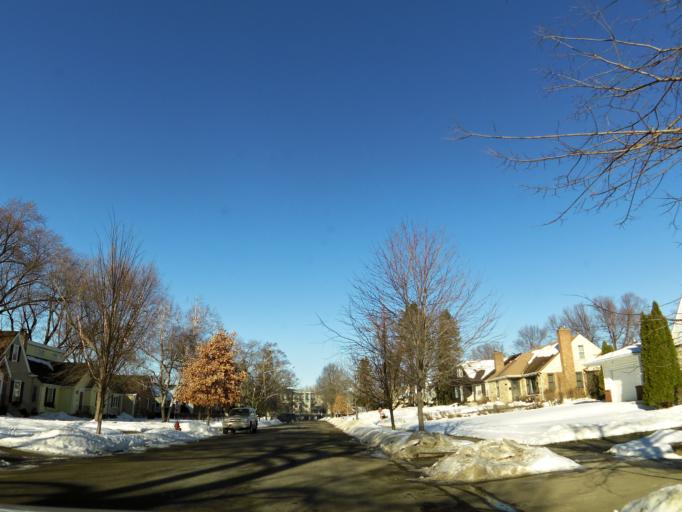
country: US
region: Minnesota
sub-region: Hennepin County
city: Saint Louis Park
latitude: 44.9371
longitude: -93.3303
